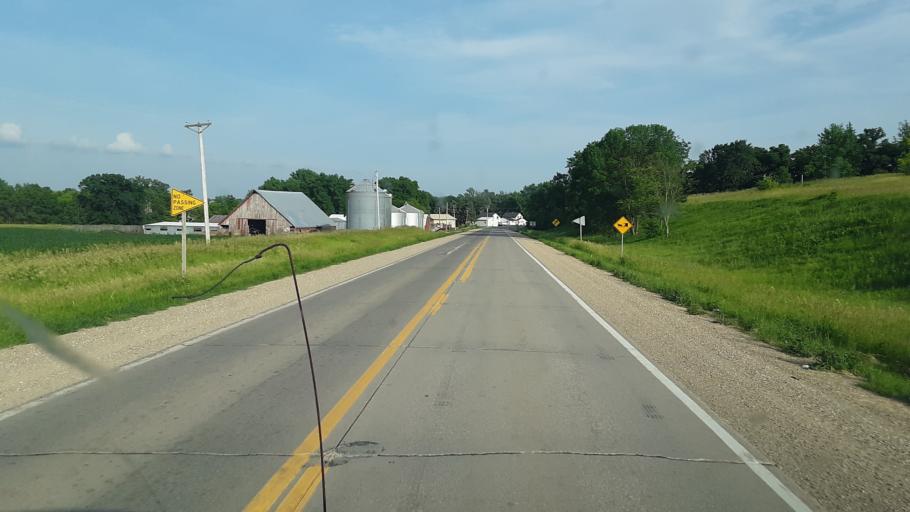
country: US
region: Iowa
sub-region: Tama County
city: Toledo
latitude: 41.9850
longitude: -92.7176
